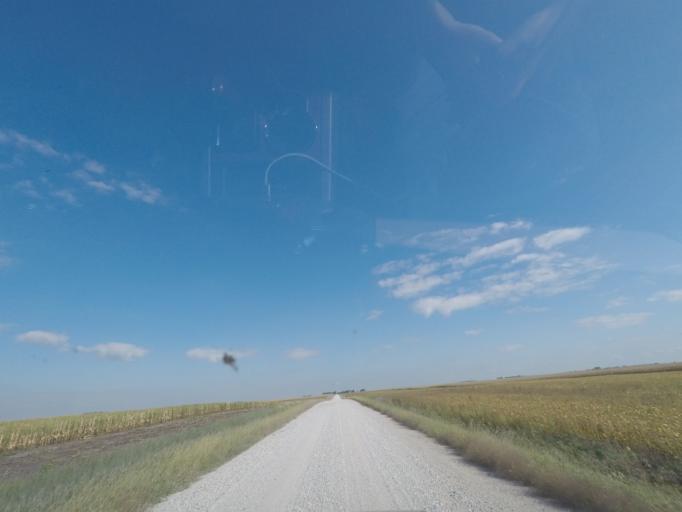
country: US
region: Iowa
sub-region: Story County
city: Nevada
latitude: 42.0432
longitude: -93.4252
